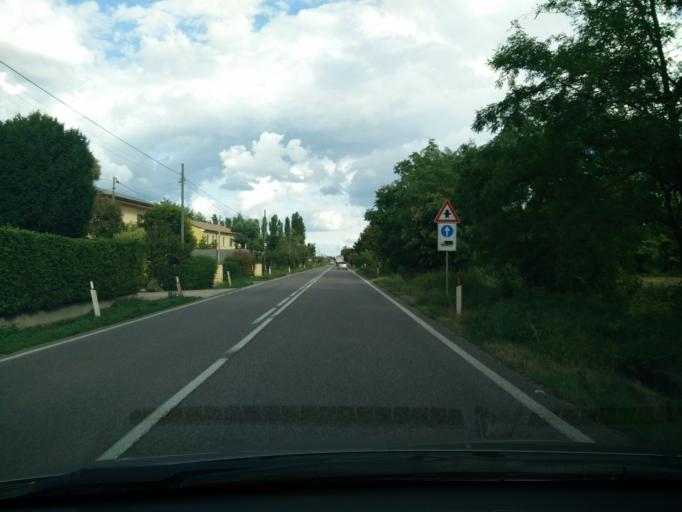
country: IT
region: Veneto
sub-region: Provincia di Treviso
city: Fossalunga
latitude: 45.7054
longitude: 12.0479
